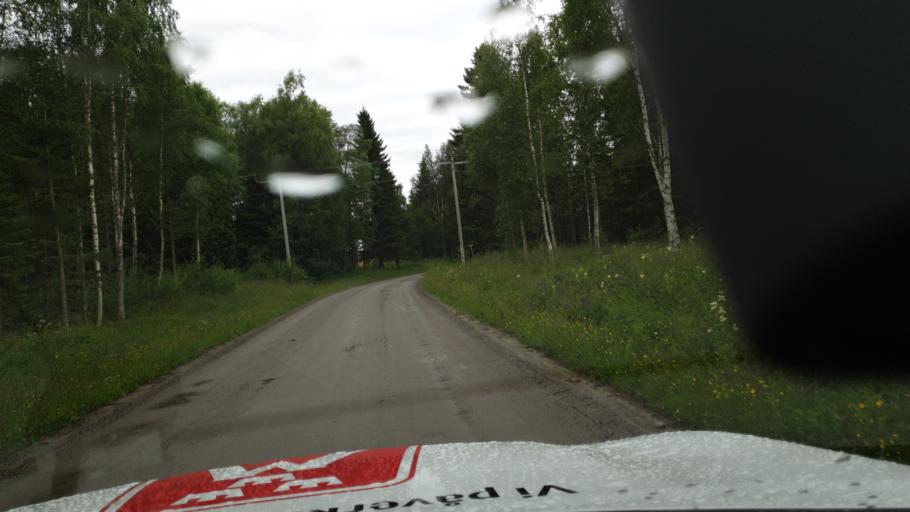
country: SE
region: Vaesterbotten
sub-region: Robertsfors Kommun
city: Robertsfors
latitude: 64.2177
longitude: 21.0752
